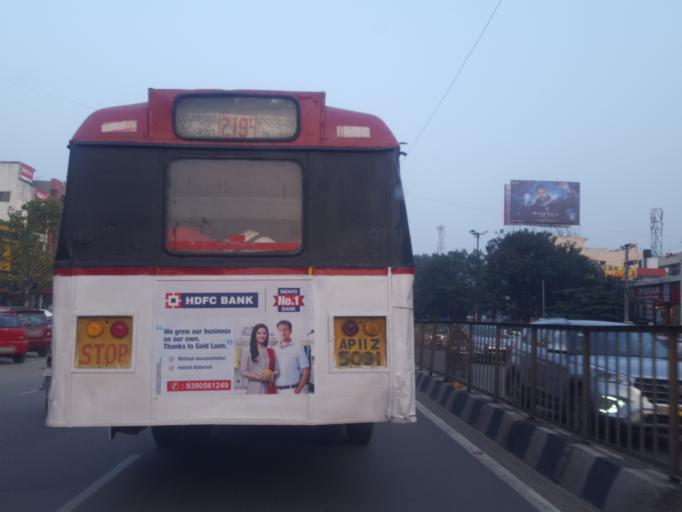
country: IN
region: Telangana
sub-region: Medak
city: Serilingampalle
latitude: 17.4953
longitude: 78.3217
